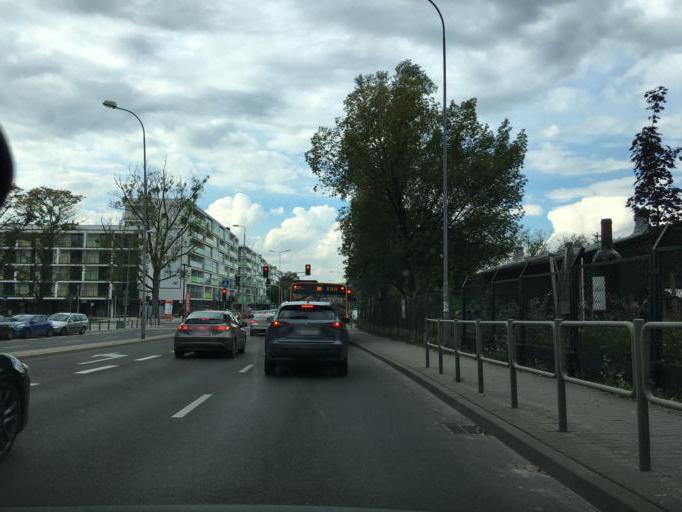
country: PL
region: Masovian Voivodeship
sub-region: Warszawa
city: Zoliborz
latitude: 52.2564
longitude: 20.9685
